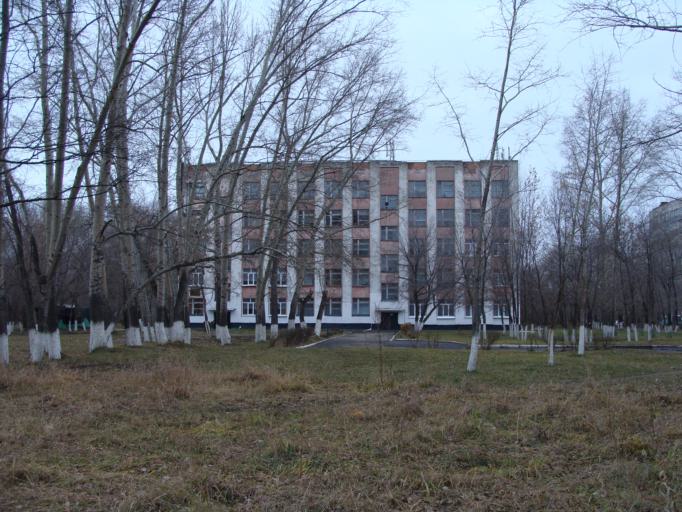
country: RU
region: Altai Krai
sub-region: Gorod Barnaulskiy
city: Barnaul
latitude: 53.3624
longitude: 83.6880
